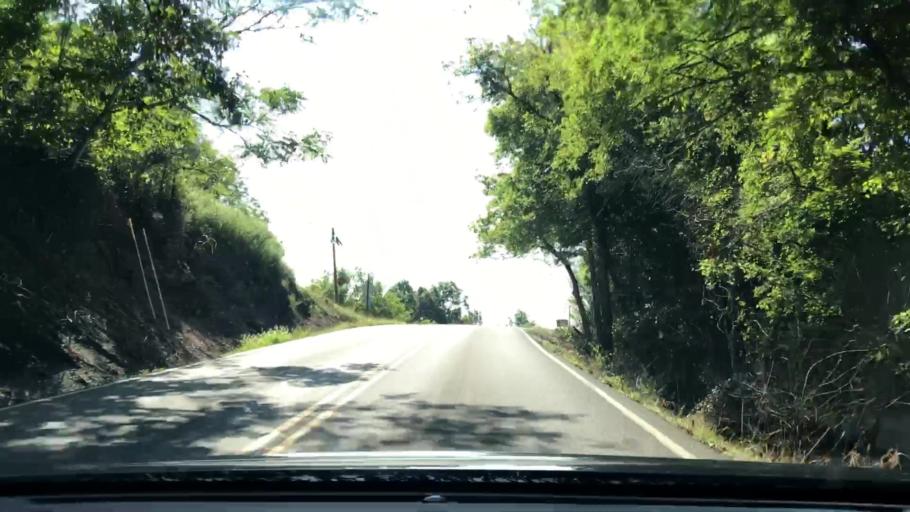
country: US
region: Tennessee
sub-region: Jackson County
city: Gainesboro
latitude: 36.3564
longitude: -85.6711
